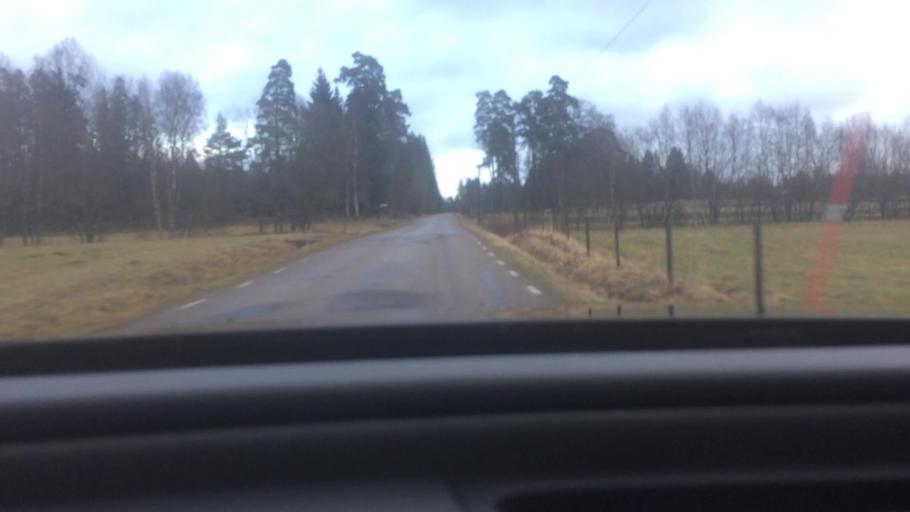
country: SE
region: Vaestra Goetaland
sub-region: Falkopings Kommun
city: Falkoeping
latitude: 57.9945
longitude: 13.4734
